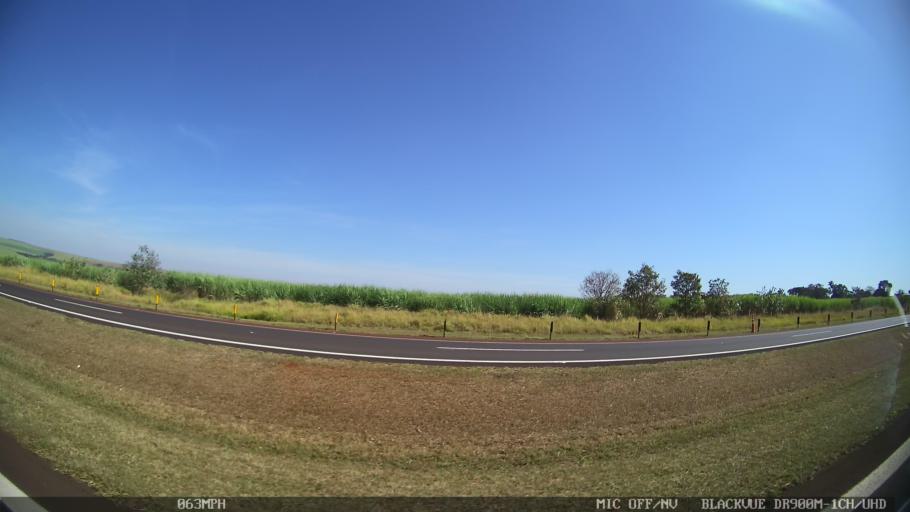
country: BR
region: Sao Paulo
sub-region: Ribeirao Preto
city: Ribeirao Preto
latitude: -21.1844
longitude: -47.8901
